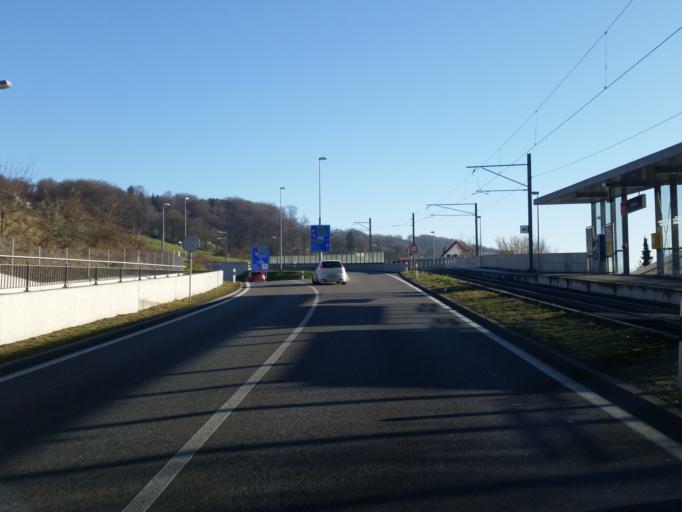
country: CH
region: Aargau
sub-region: Bezirk Bremgarten
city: Bremgarten
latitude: 47.3528
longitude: 8.3546
